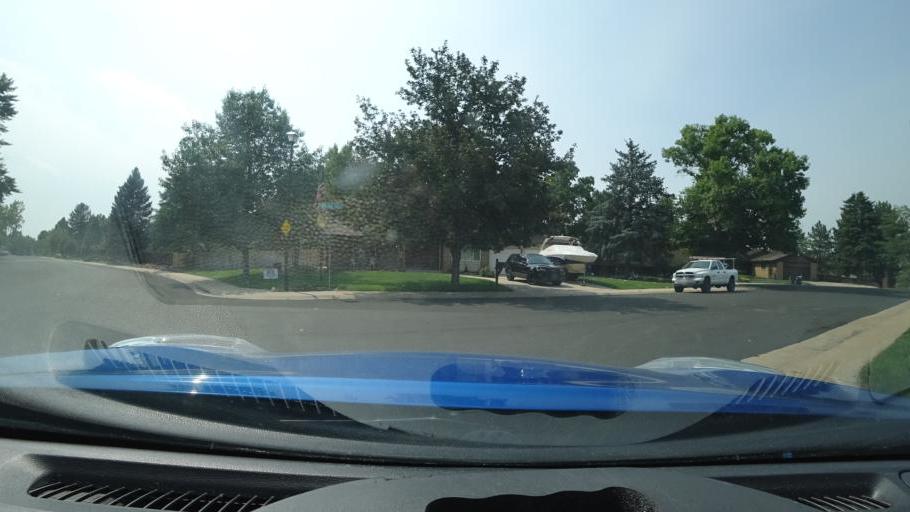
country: US
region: Colorado
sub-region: Adams County
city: Aurora
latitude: 39.6739
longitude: -104.8554
